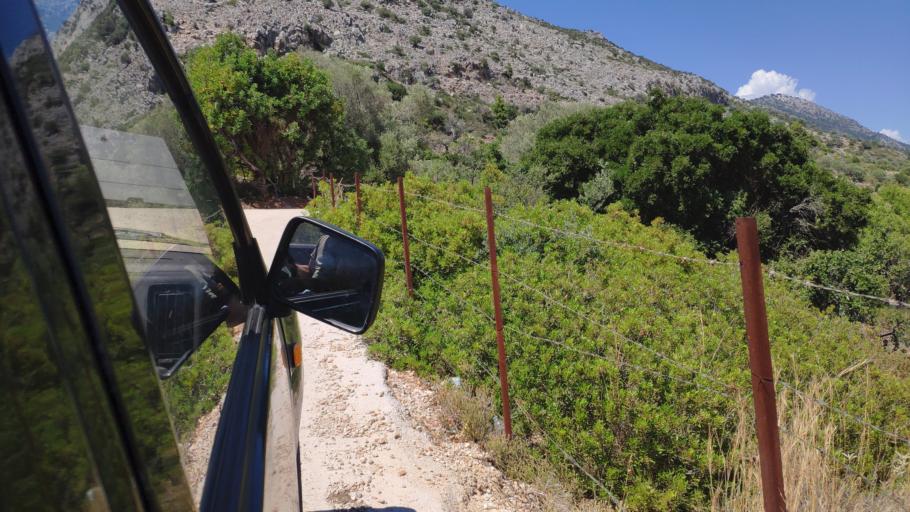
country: GR
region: West Greece
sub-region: Nomos Aitolias kai Akarnanias
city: Kandila
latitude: 38.6191
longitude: 20.9188
